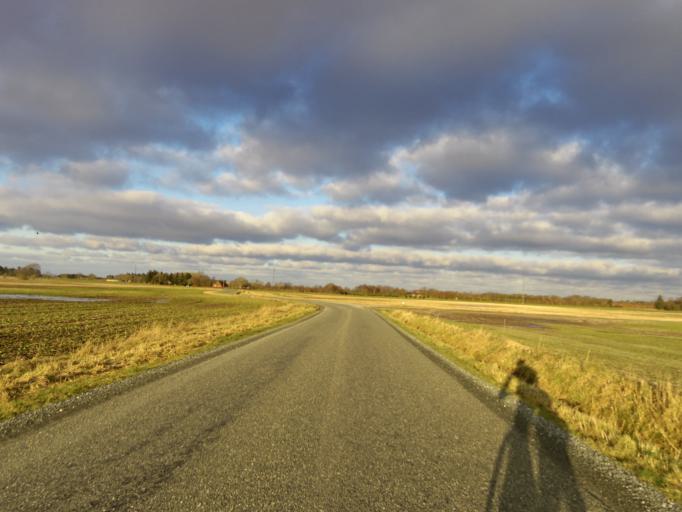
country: DK
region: South Denmark
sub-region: Esbjerg Kommune
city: Ribe
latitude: 55.2866
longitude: 8.8464
